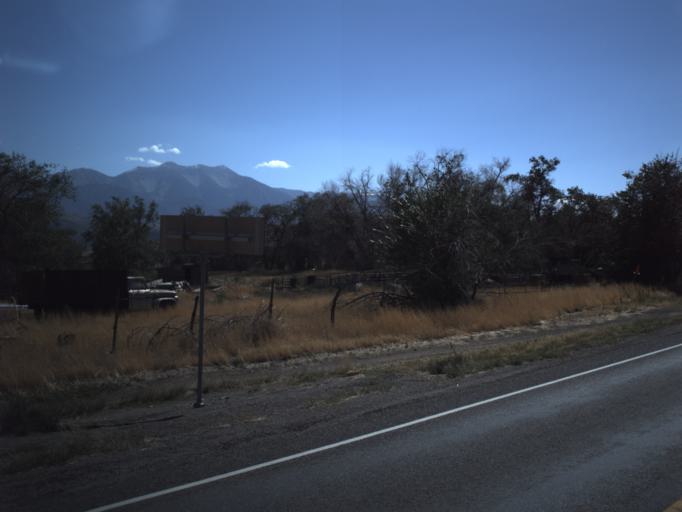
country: US
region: Utah
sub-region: Utah County
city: Genola
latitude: 39.9542
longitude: -111.9563
